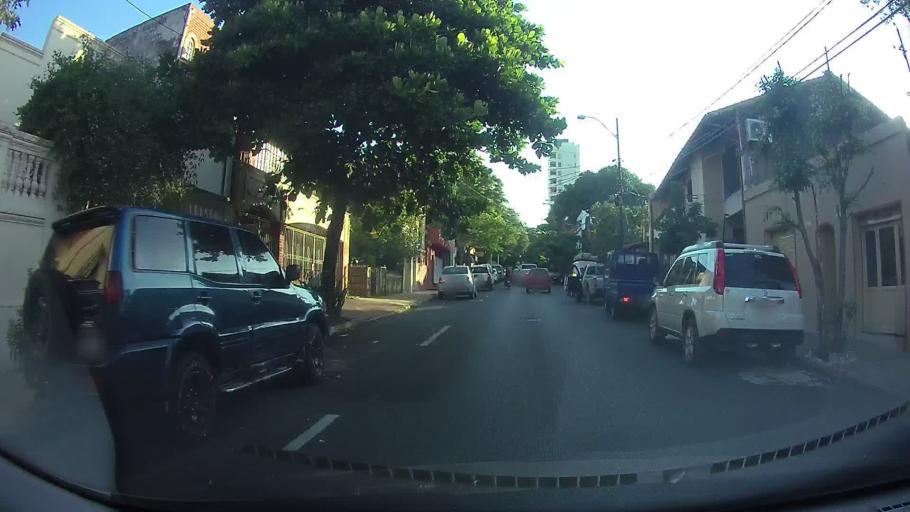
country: PY
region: Asuncion
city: Asuncion
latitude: -25.2923
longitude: -57.6349
